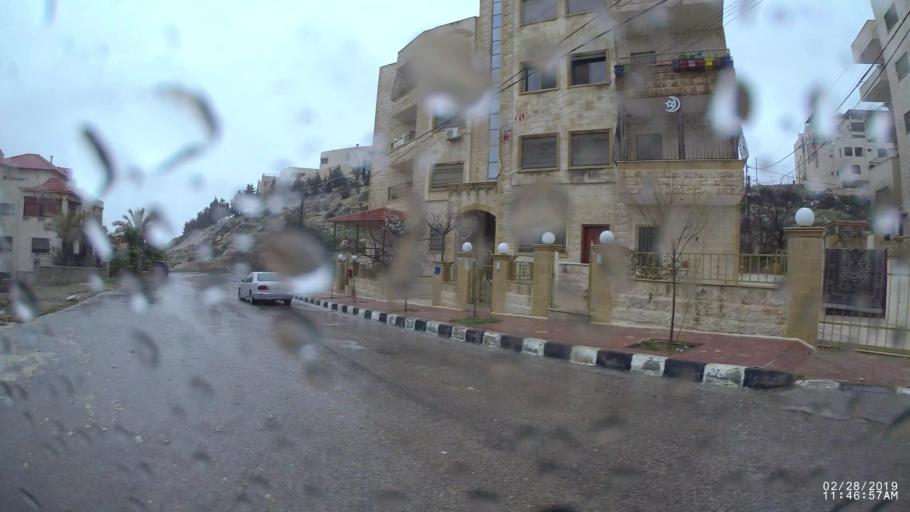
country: JO
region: Amman
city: Al Jubayhah
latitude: 32.0184
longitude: 35.8899
